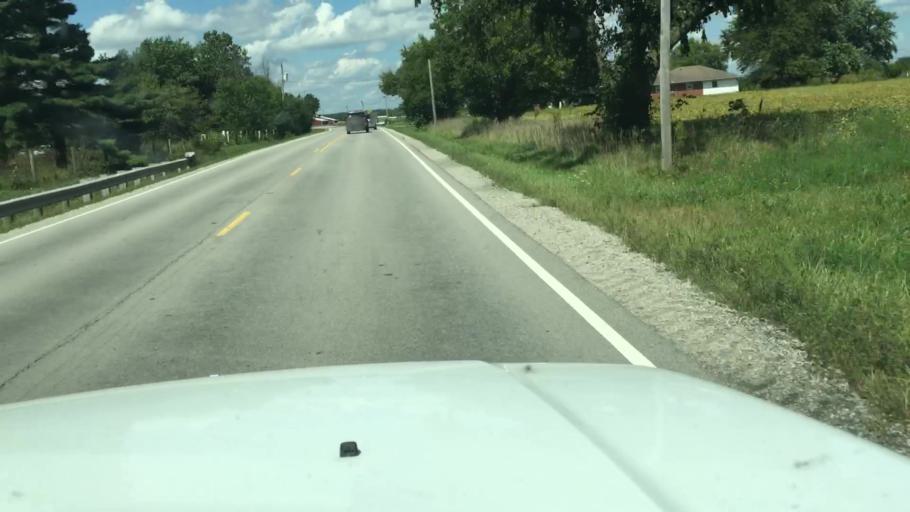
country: US
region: Ohio
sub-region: Madison County
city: Mount Sterling
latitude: 39.7375
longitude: -83.2748
